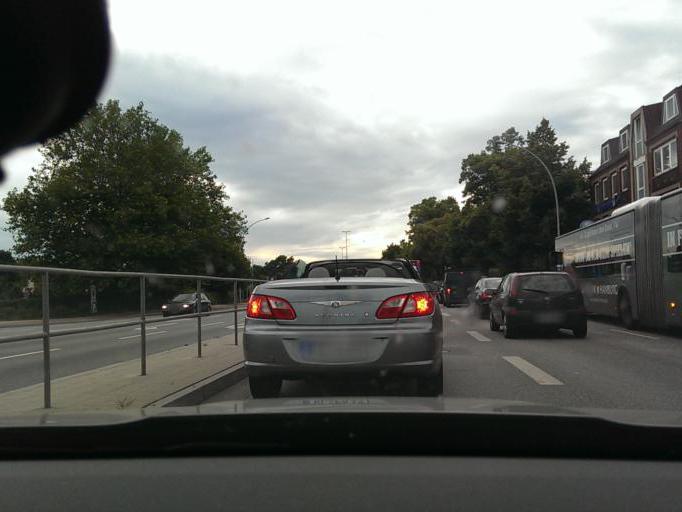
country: DE
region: Hamburg
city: Stellingen
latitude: 53.5931
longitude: 9.9275
